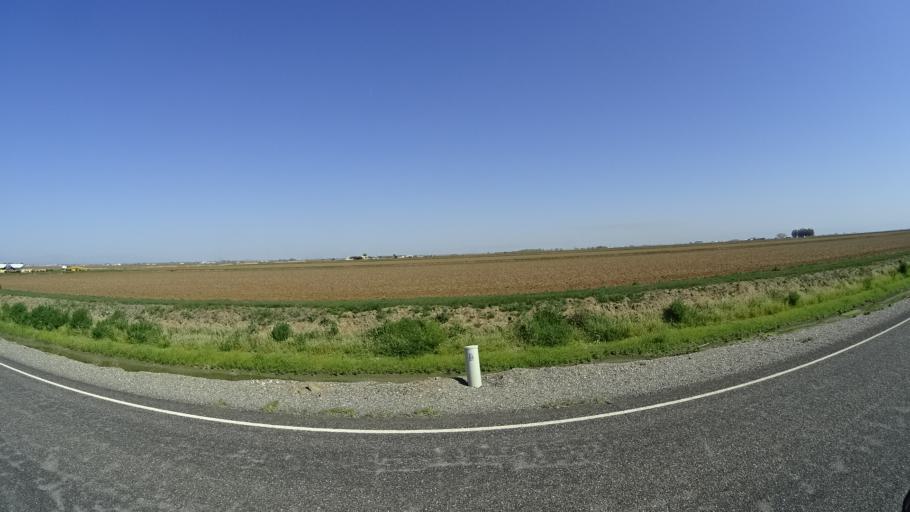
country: US
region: California
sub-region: Glenn County
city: Willows
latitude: 39.4659
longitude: -122.1533
